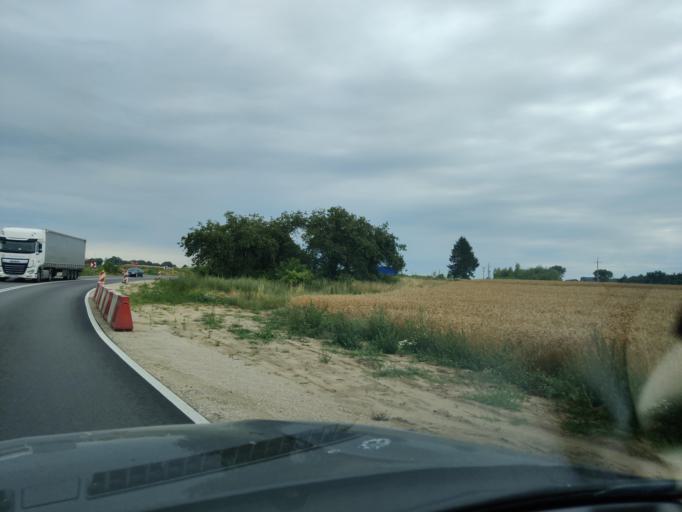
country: PL
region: Masovian Voivodeship
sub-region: Powiat ostrowski
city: Ostrow Mazowiecka
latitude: 52.8196
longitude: 21.9127
